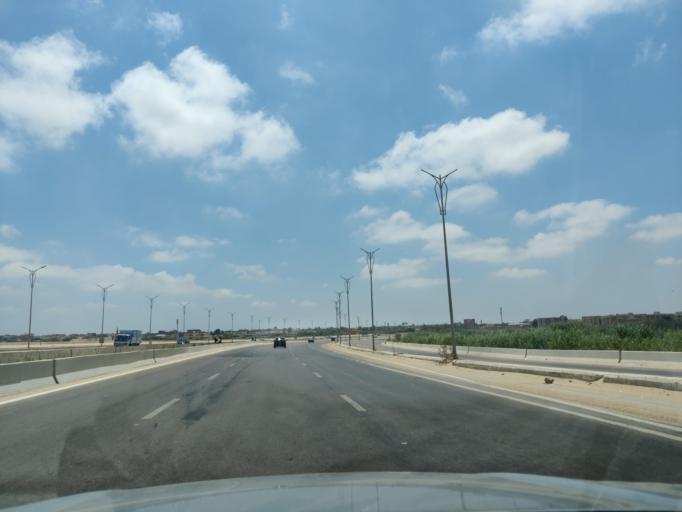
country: EG
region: Alexandria
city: Alexandria
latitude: 30.9866
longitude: 29.6561
